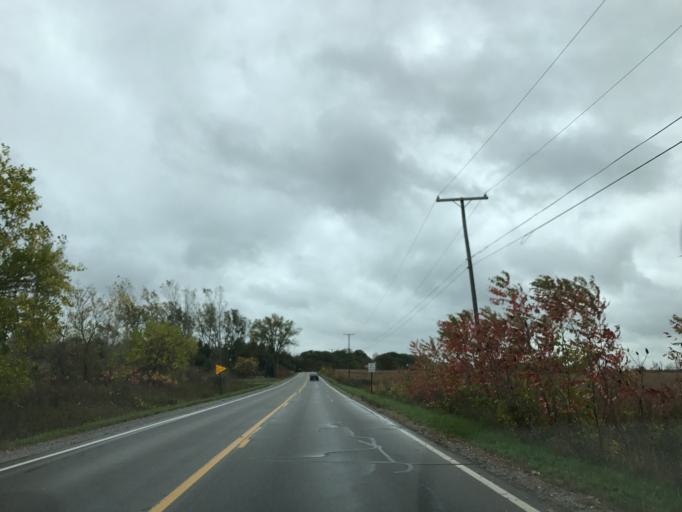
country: US
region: Michigan
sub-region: Oakland County
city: South Lyon
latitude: 42.3871
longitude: -83.6449
